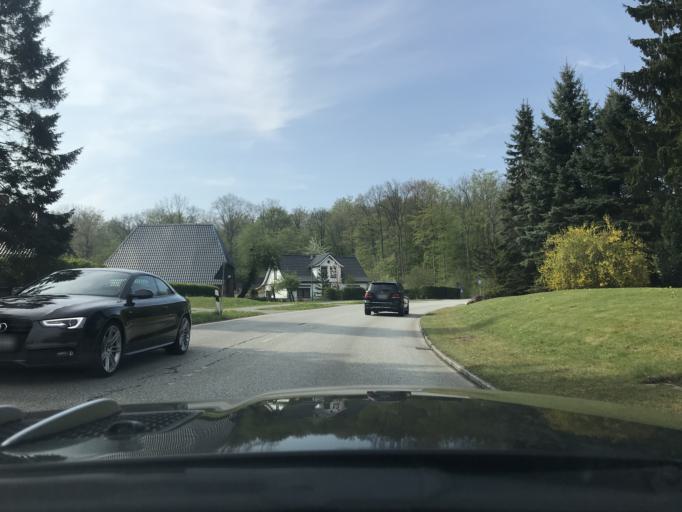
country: DE
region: Schleswig-Holstein
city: Gromitz
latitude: 54.1804
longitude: 10.9816
